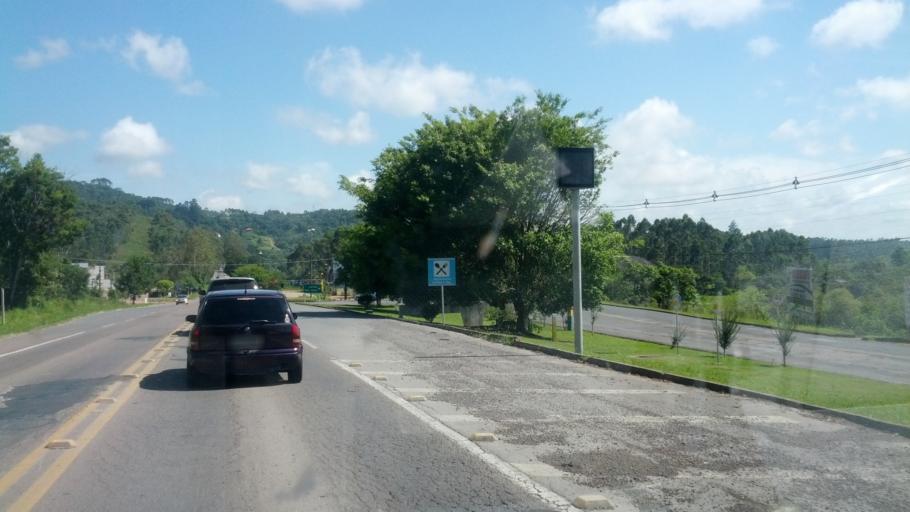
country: BR
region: Santa Catarina
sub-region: Rio Do Sul
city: Rio do Sul
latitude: -27.1616
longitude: -49.5566
